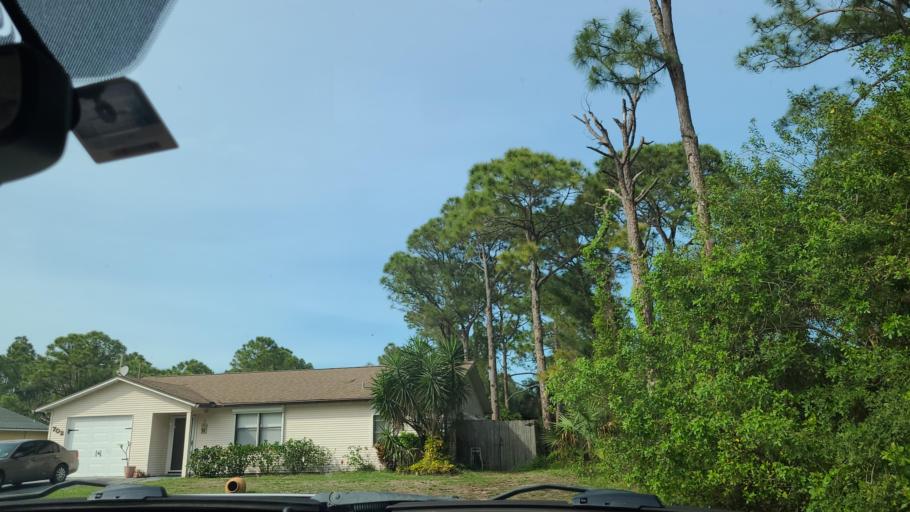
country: US
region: Florida
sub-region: Indian River County
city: Sebastian
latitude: 27.7894
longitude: -80.4867
